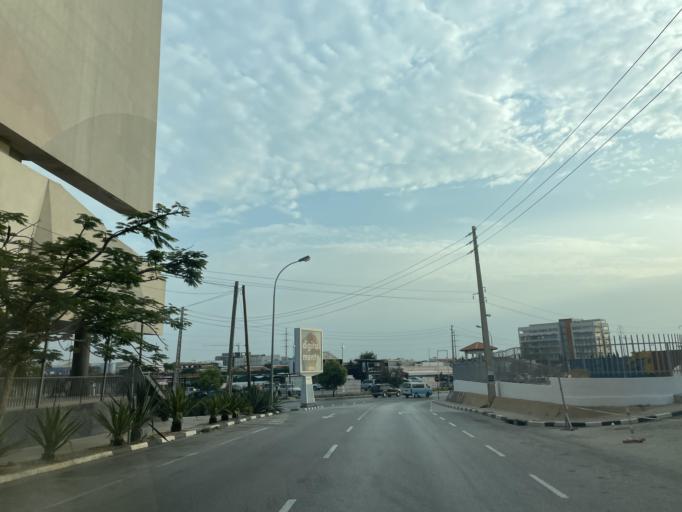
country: AO
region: Luanda
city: Luanda
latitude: -8.9190
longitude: 13.1848
